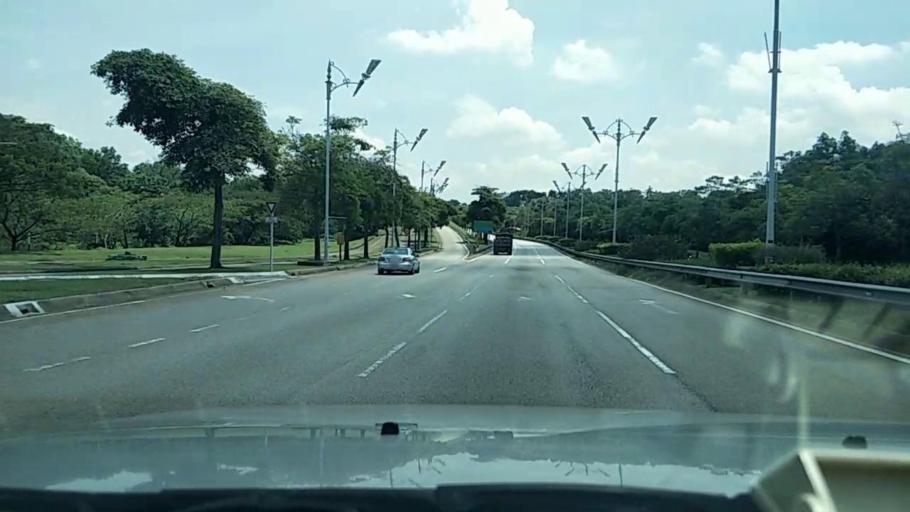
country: MY
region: Putrajaya
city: Putrajaya
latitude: 2.9553
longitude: 101.6933
